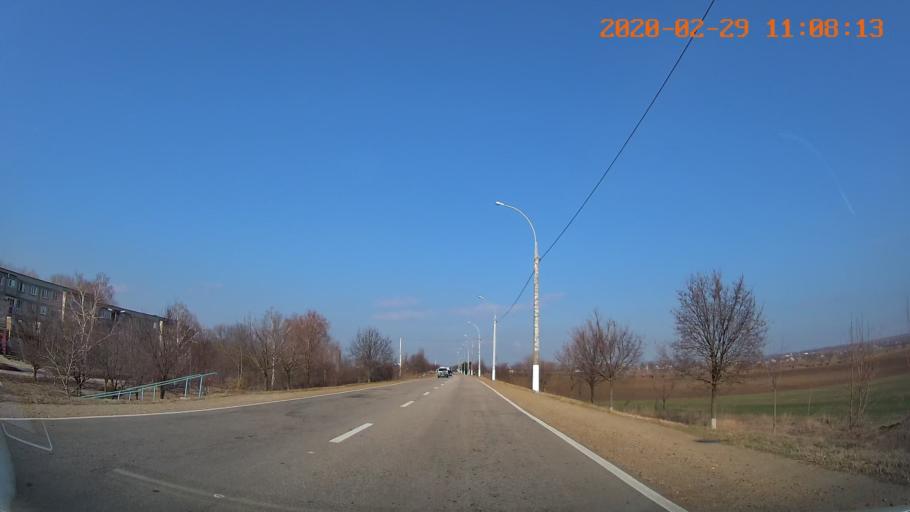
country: MD
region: Criuleni
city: Criuleni
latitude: 47.2320
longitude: 29.1772
